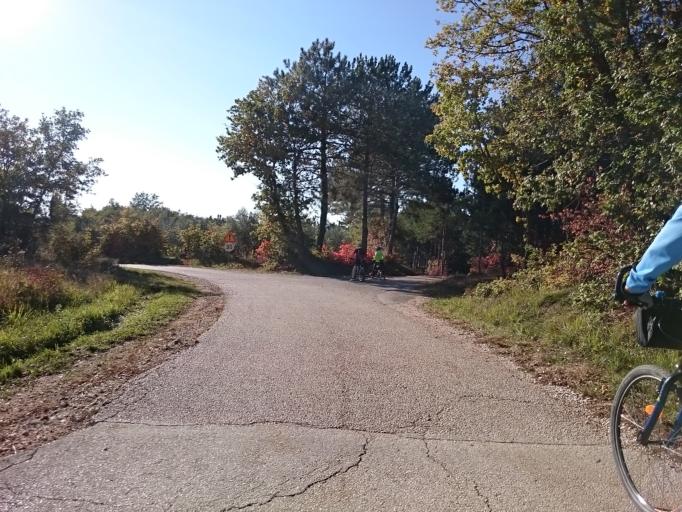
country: HR
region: Istarska
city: Buje
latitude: 45.4224
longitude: 13.7342
